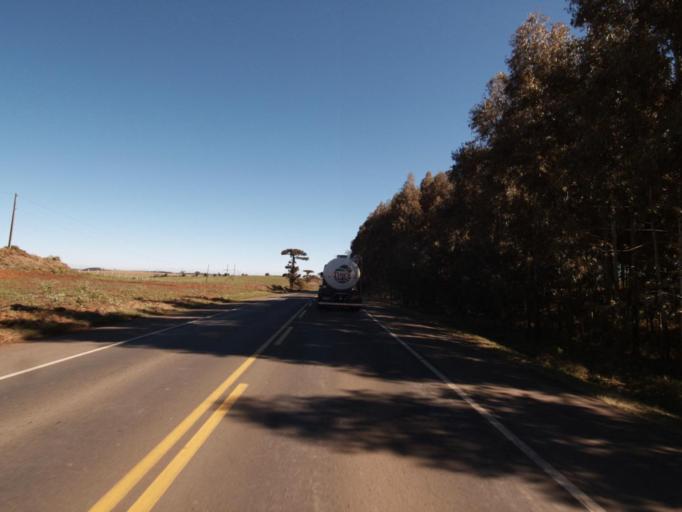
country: BR
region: Santa Catarina
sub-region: Xanxere
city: Xanxere
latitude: -26.8766
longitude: -52.3305
